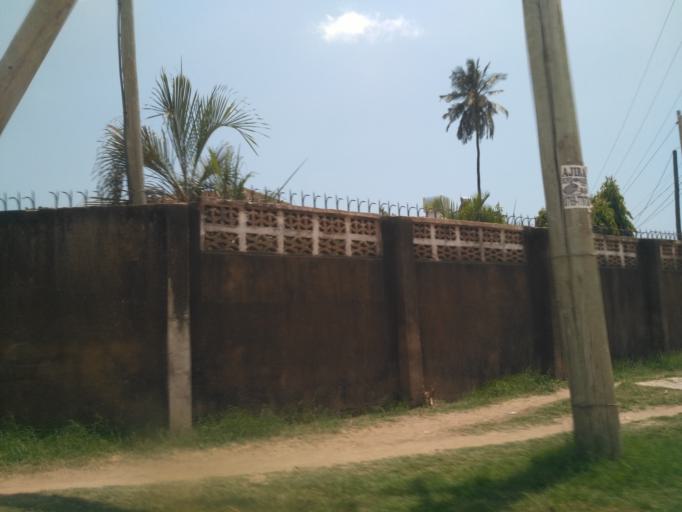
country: TZ
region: Dar es Salaam
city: Dar es Salaam
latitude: -6.8016
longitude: 39.2803
